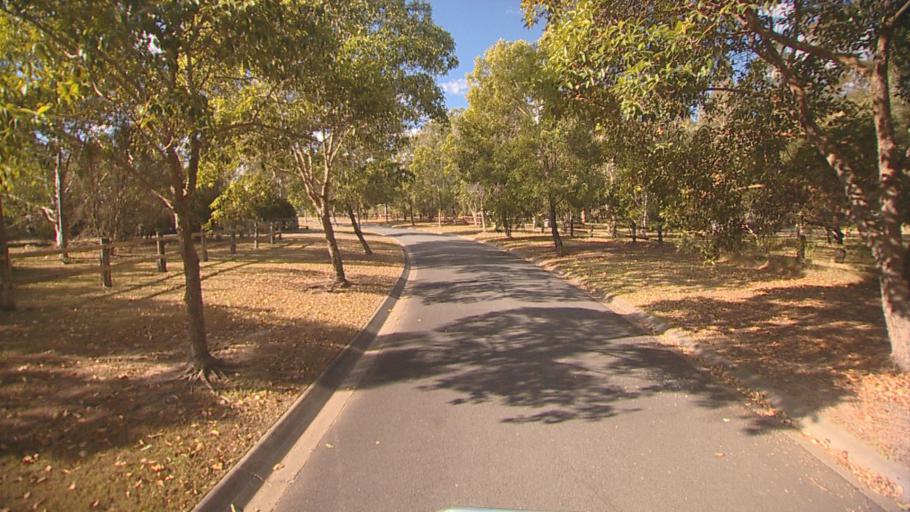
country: AU
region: Queensland
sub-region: Logan
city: North Maclean
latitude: -27.8023
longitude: 152.9691
